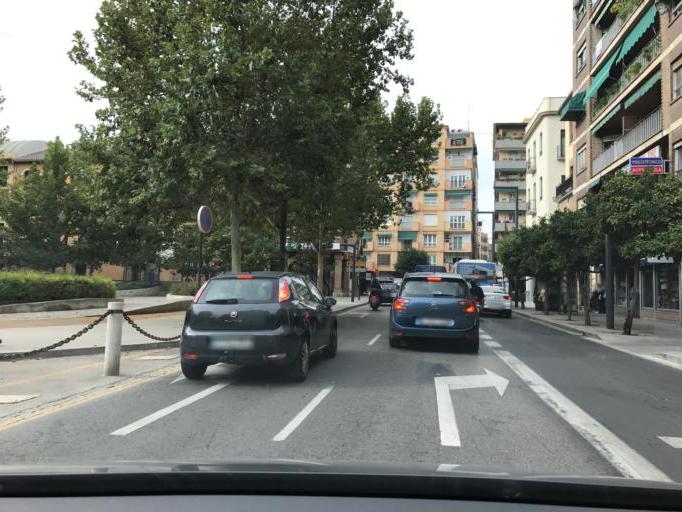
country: ES
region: Andalusia
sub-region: Provincia de Granada
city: Granada
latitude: 37.1695
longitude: -3.5961
